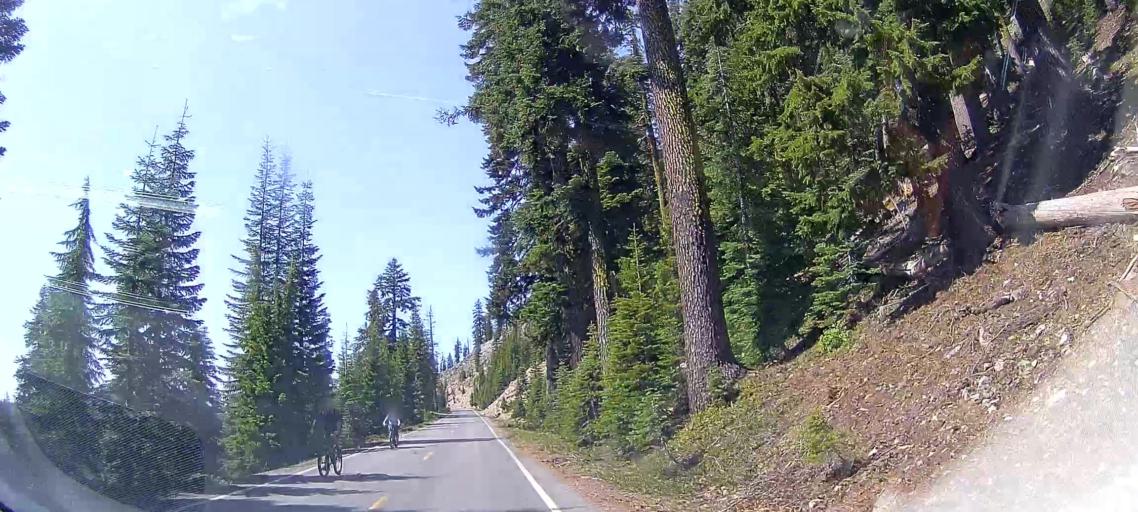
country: US
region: Oregon
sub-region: Klamath County
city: Klamath Falls
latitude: 42.8800
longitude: -122.1026
